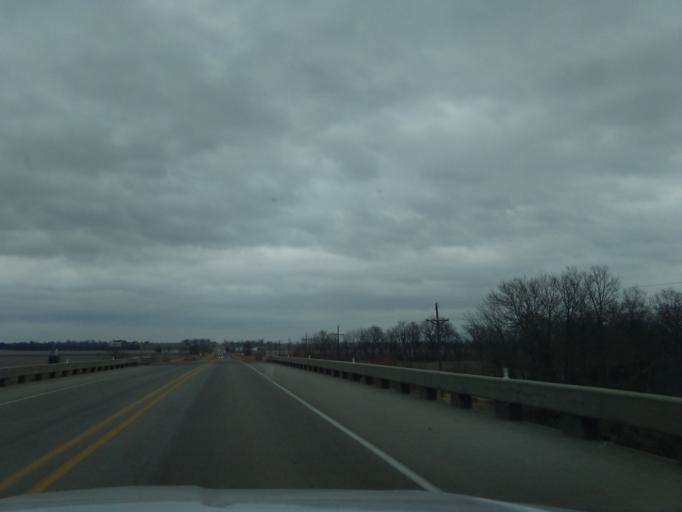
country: US
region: Nebraska
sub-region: Nemaha County
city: Auburn
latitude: 40.3926
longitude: -95.8137
